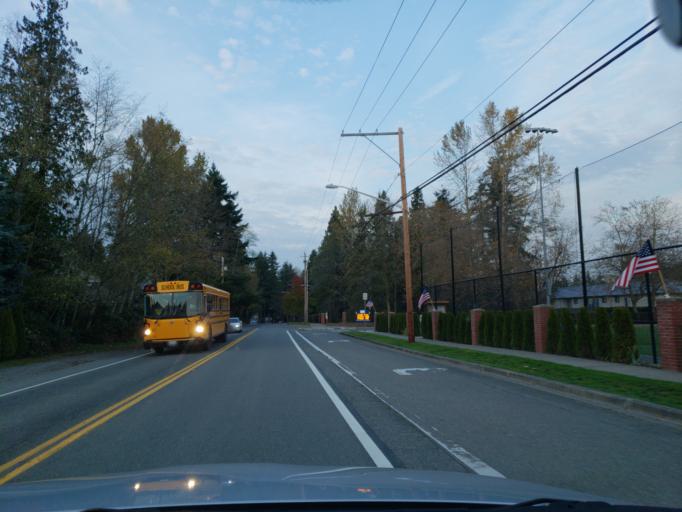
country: US
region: Washington
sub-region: King County
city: Bothell
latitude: 47.7455
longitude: -122.1915
